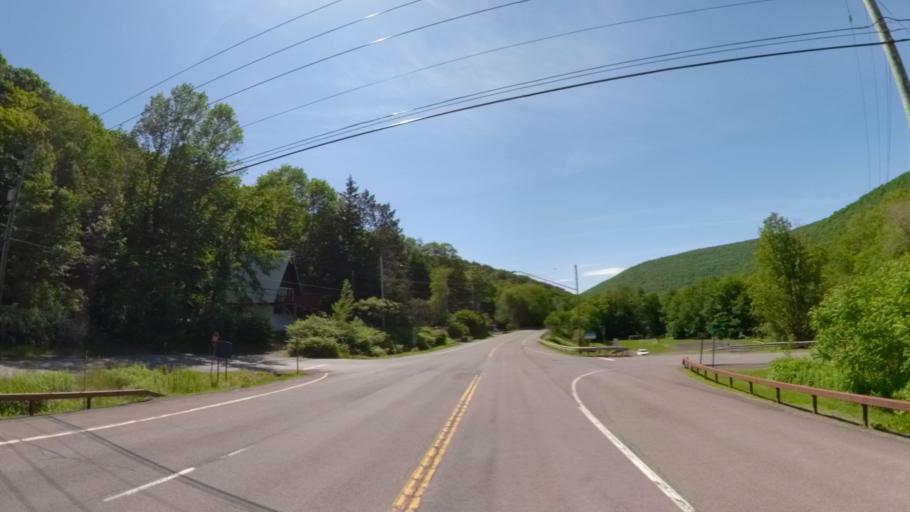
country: US
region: New York
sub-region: Delaware County
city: Stamford
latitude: 42.1345
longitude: -74.4778
